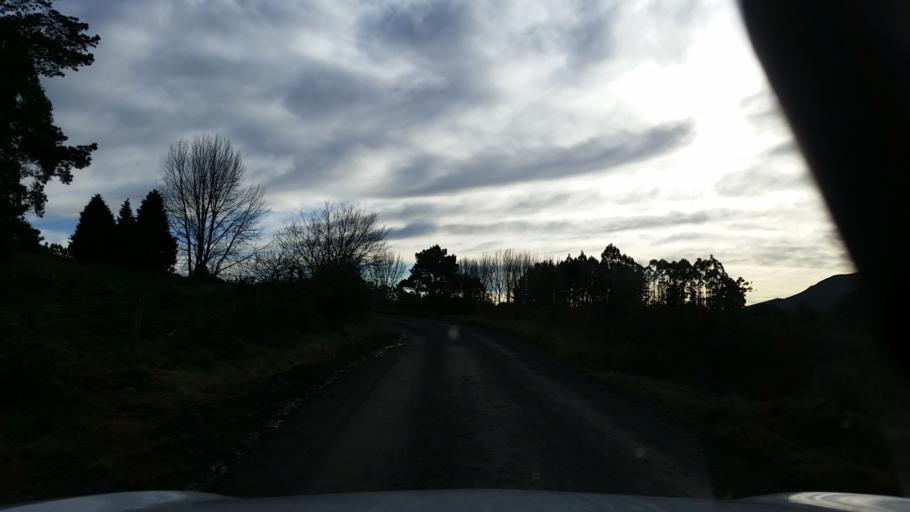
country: NZ
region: Bay of Plenty
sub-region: Rotorua District
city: Rotorua
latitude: -38.2629
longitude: 176.1595
